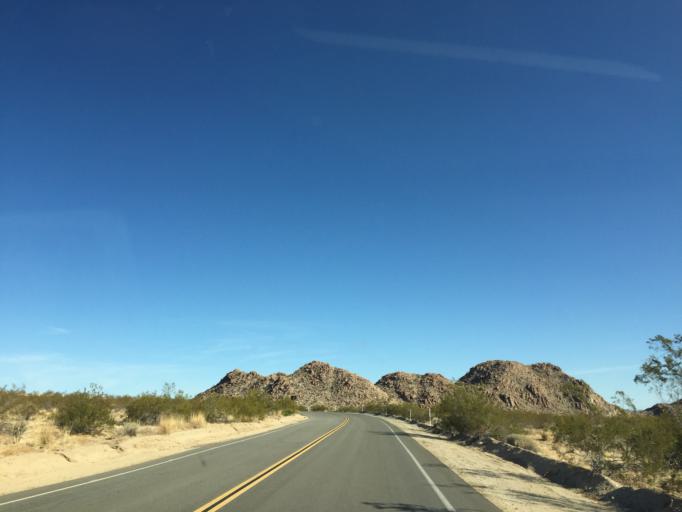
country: US
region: California
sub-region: Riverside County
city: Mecca
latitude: 33.8286
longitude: -115.7593
